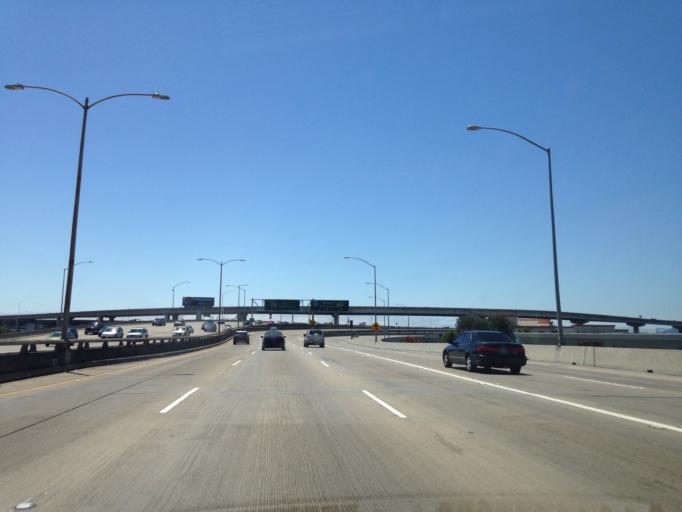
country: US
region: California
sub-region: Alameda County
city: Emeryville
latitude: 37.8272
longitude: -122.2856
